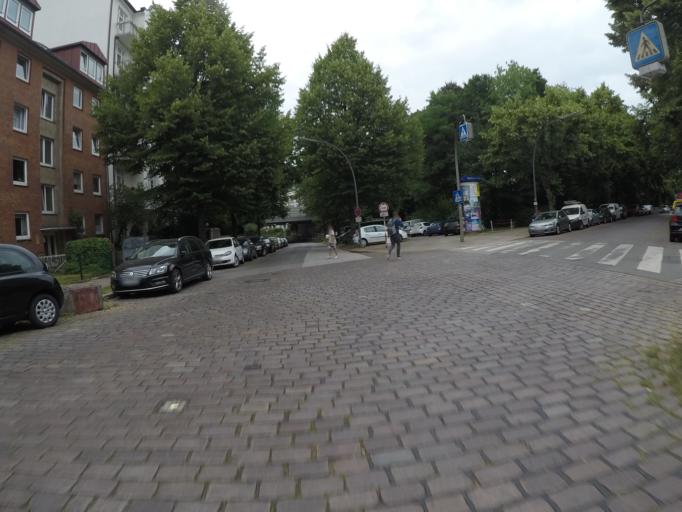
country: DE
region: Hamburg
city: Borgfelde
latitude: 53.5621
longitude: 10.0429
